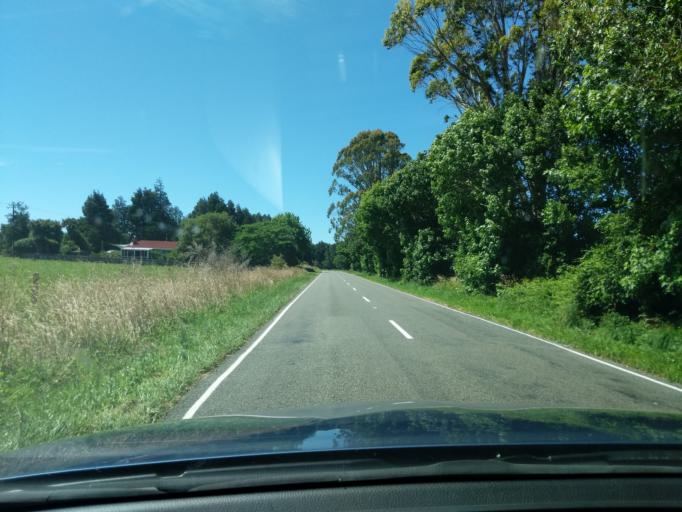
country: NZ
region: Tasman
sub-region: Tasman District
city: Takaka
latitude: -40.7023
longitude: 172.6334
